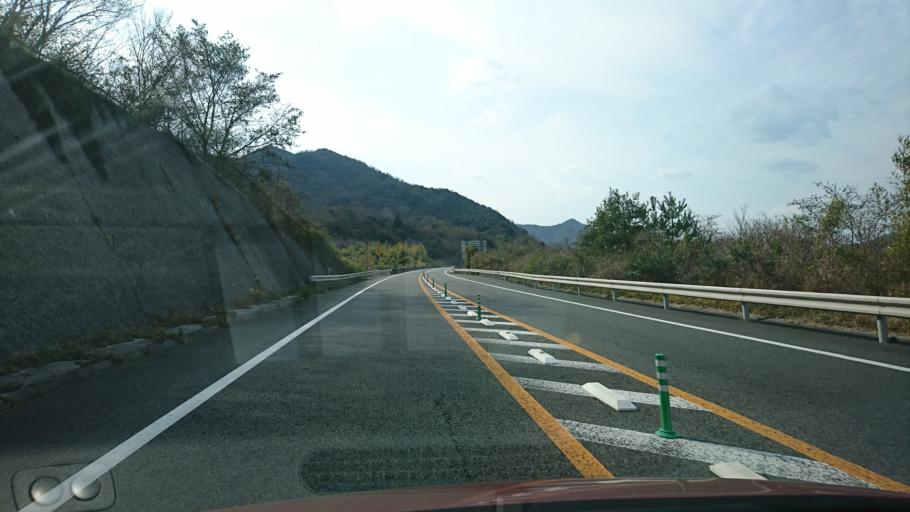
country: JP
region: Hiroshima
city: Innoshima
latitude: 34.1362
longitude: 133.0526
